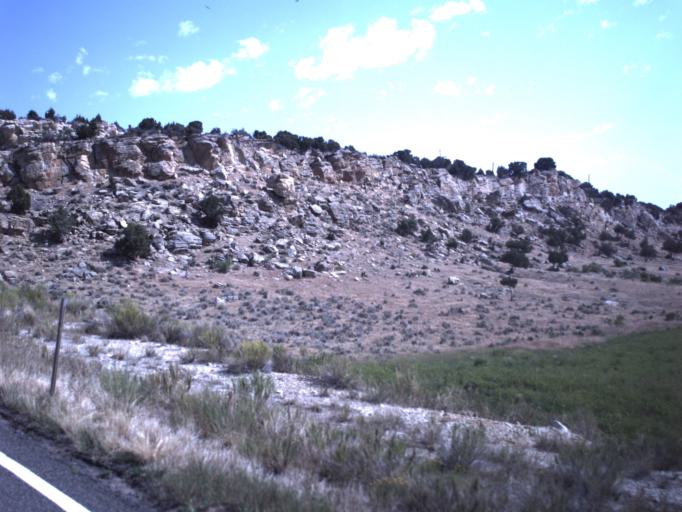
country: US
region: Utah
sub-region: Daggett County
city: Manila
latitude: 40.9534
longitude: -109.7126
